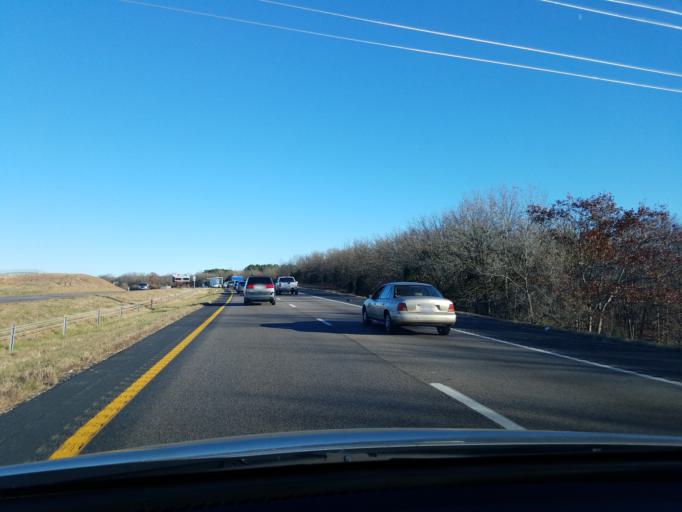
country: US
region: Missouri
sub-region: Phelps County
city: Rolla
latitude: 37.9758
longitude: -91.7389
